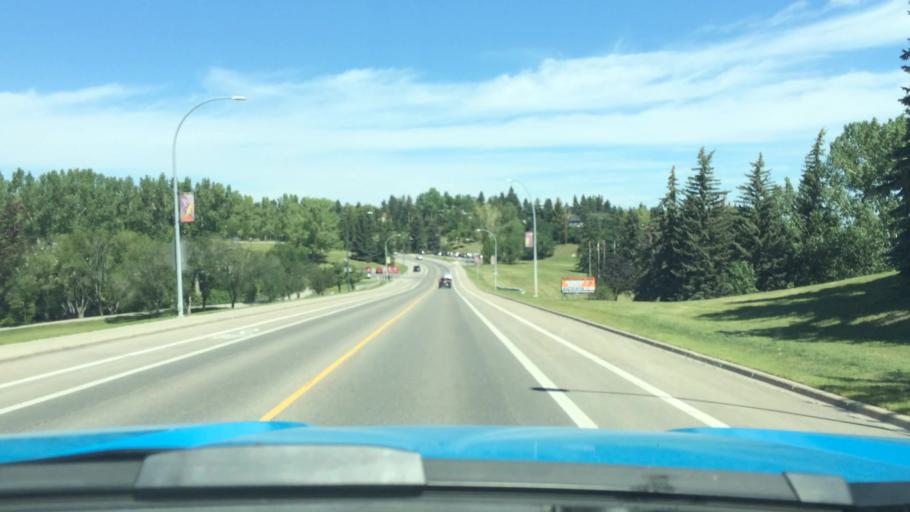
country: CA
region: Alberta
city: Calgary
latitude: 51.0747
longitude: -114.0846
